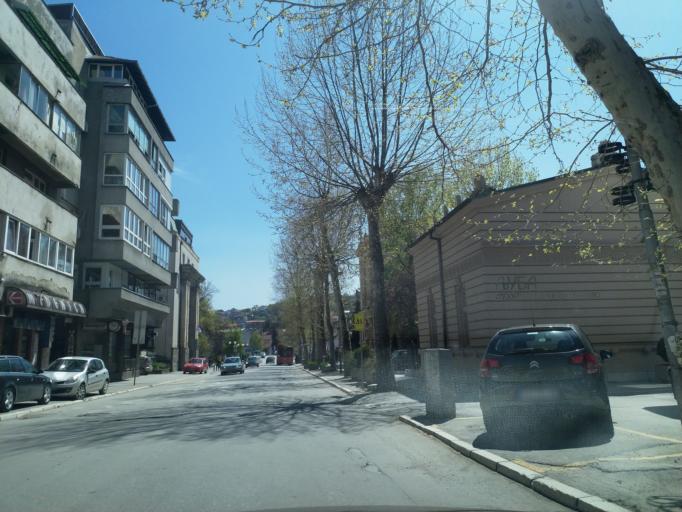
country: RS
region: Central Serbia
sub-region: Kolubarski Okrug
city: Valjevo
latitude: 44.2704
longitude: 19.8863
